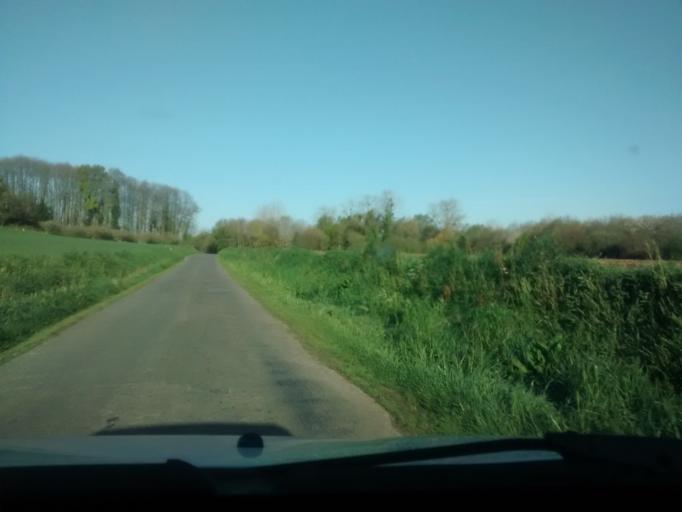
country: FR
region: Brittany
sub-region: Departement d'Ille-et-Vilaine
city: Roz-sur-Couesnon
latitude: 48.5530
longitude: -1.5984
